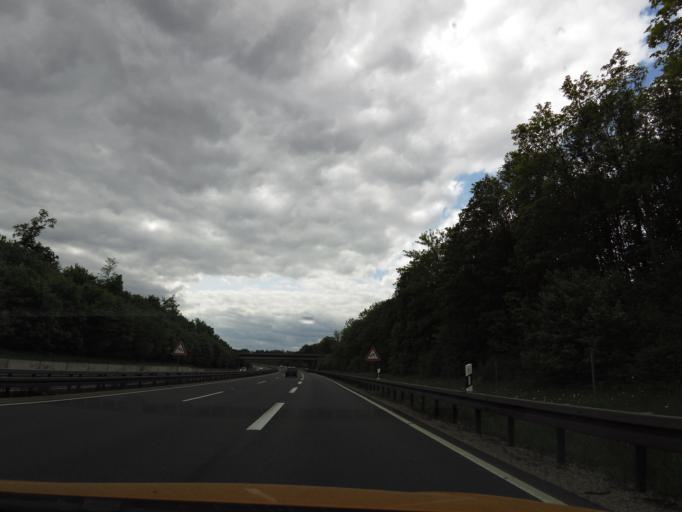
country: DE
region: Lower Saxony
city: Holle
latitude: 52.1091
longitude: 10.1874
